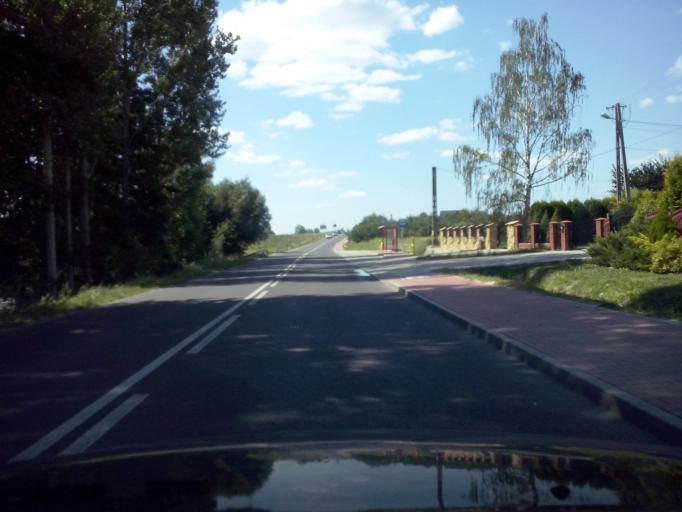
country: PL
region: Swietokrzyskie
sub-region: Powiat buski
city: Gnojno
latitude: 50.5997
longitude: 20.8609
